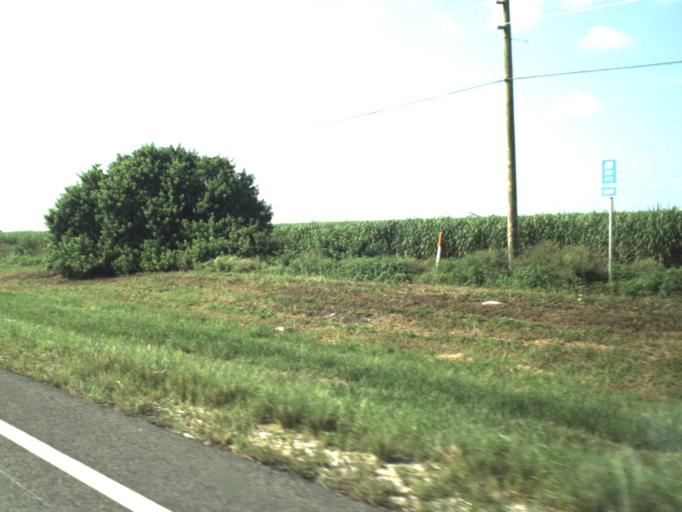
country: US
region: Florida
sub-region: Palm Beach County
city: Belle Glade Camp
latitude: 26.5116
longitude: -80.6749
